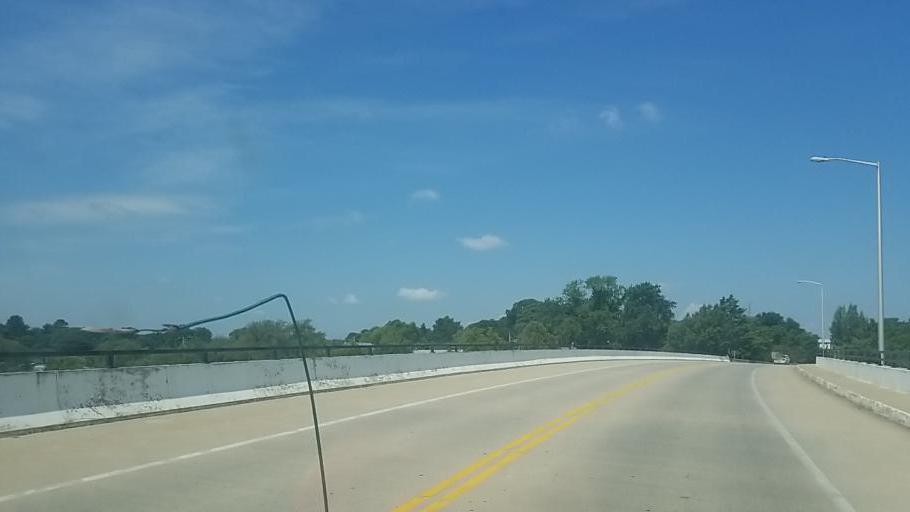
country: US
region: Maryland
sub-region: Caroline County
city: Denton
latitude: 38.8881
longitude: -75.8383
